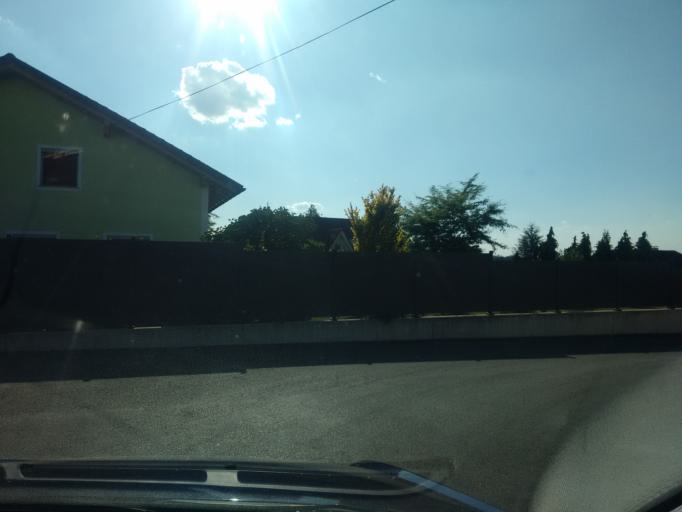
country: AT
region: Upper Austria
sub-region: Wels-Land
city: Steinhaus
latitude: 48.1241
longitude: 14.0165
